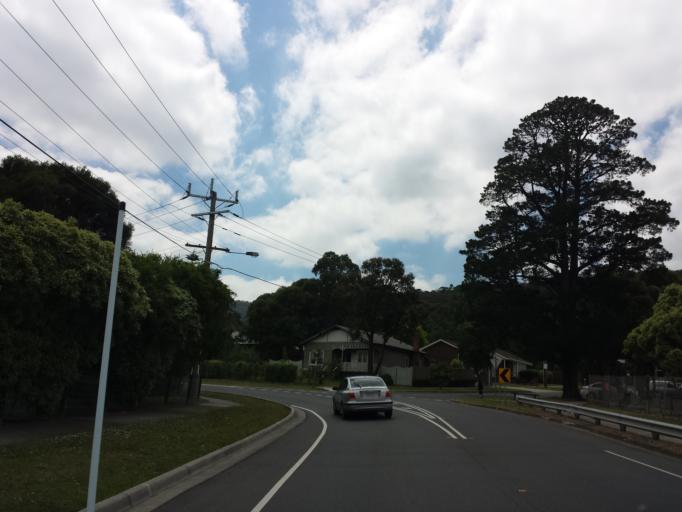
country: AU
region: Victoria
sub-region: Knox
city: Ferntree Gully
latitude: -37.8815
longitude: 145.2982
